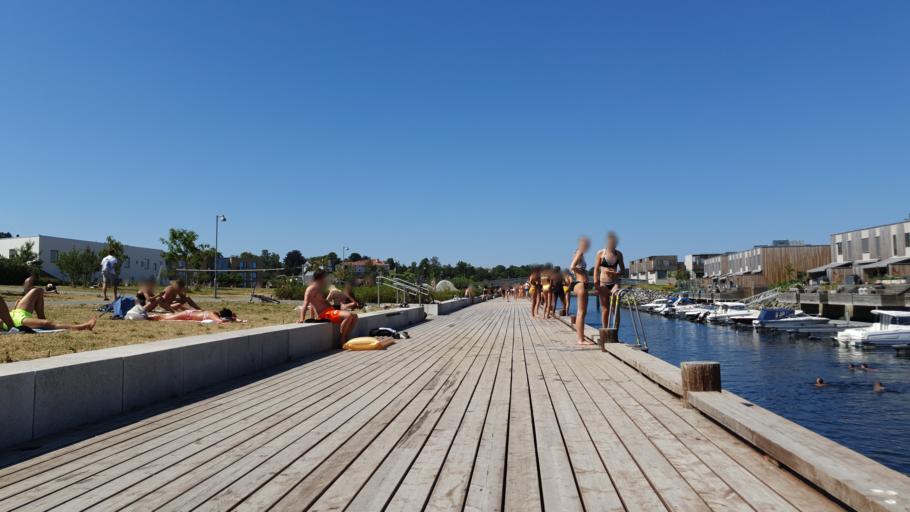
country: NO
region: Sor-Trondelag
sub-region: Trondheim
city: Trondheim
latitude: 63.4363
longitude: 10.5070
